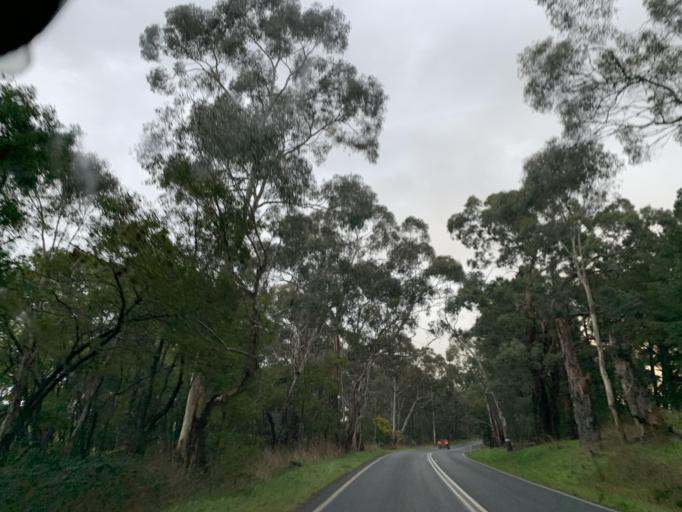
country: AU
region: Victoria
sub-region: Murrindindi
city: Kinglake West
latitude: -37.2209
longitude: 145.1228
